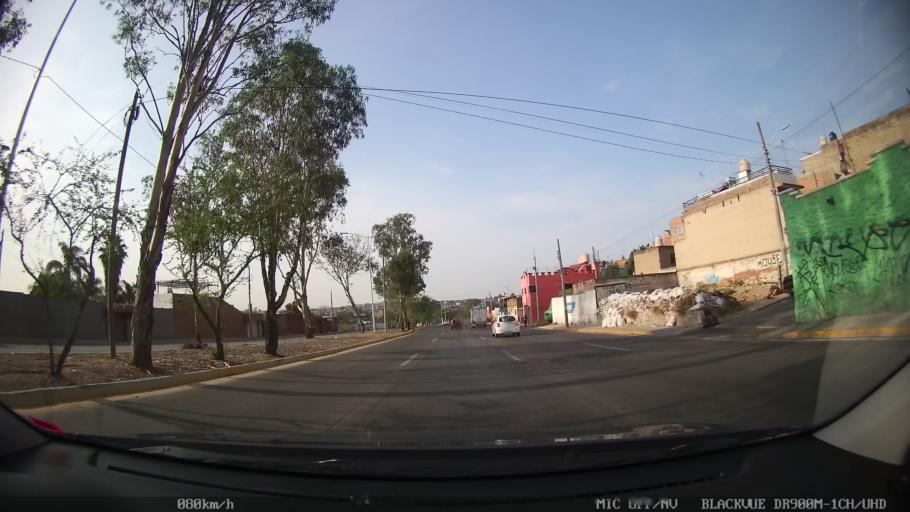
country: MX
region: Jalisco
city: Tlaquepaque
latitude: 20.7099
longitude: -103.2871
